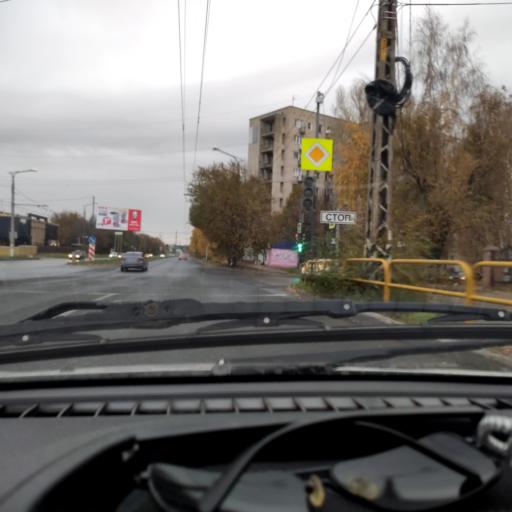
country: RU
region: Samara
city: Tol'yatti
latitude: 53.5149
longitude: 49.4409
